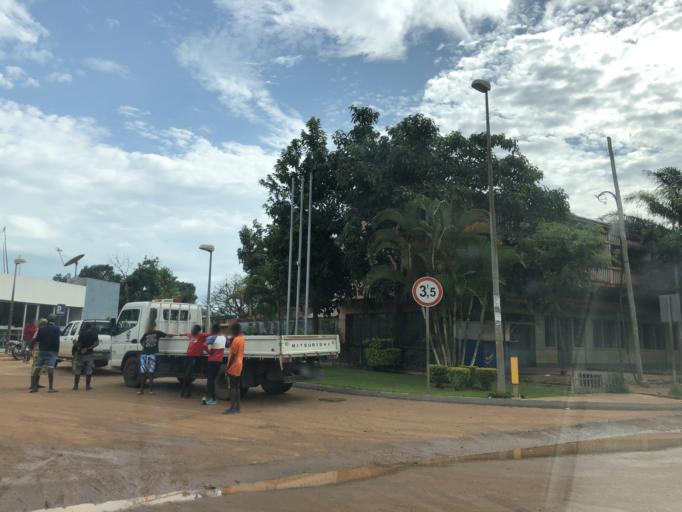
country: AO
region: Cuanza Sul
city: Uacu Cungo
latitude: -11.3623
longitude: 15.1198
